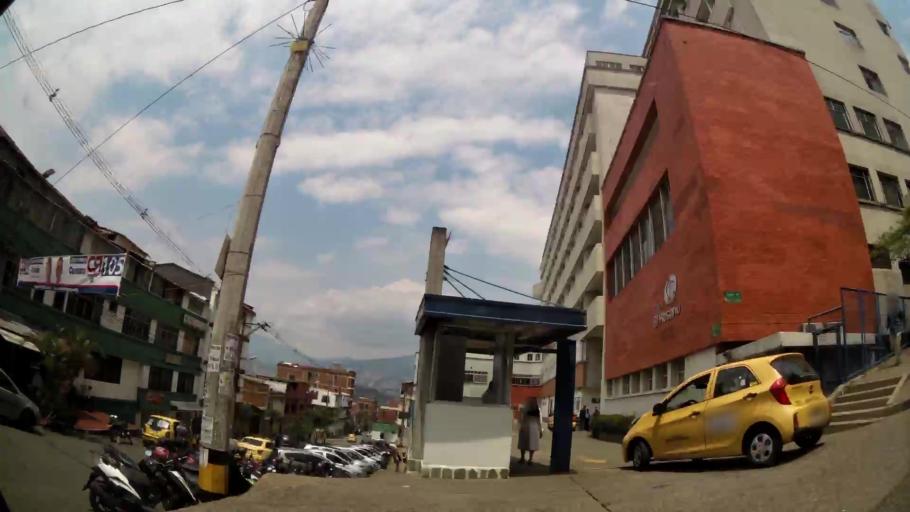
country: CO
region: Antioquia
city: Medellin
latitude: 6.2550
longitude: -75.5565
